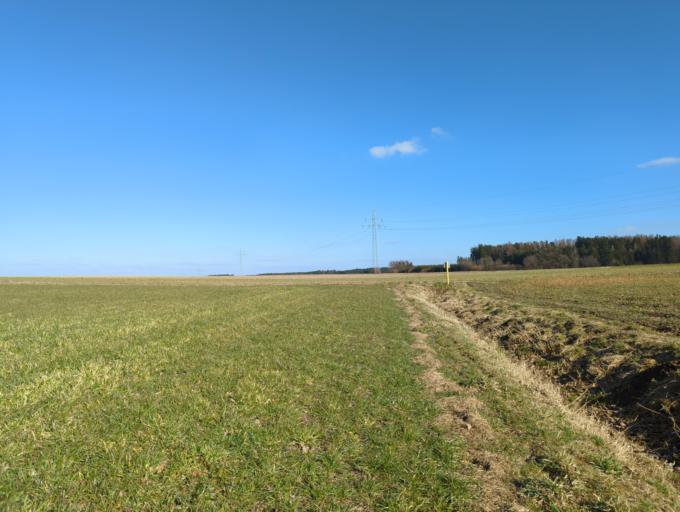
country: DE
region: Bavaria
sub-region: Swabia
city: Rettenbach
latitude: 48.4198
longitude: 10.3234
